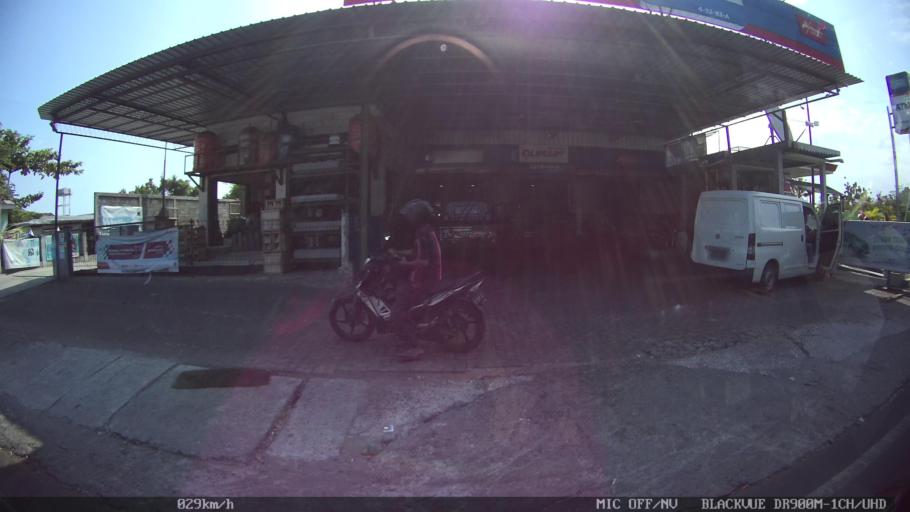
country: ID
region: Daerah Istimewa Yogyakarta
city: Sewon
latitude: -7.9155
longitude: 110.3823
